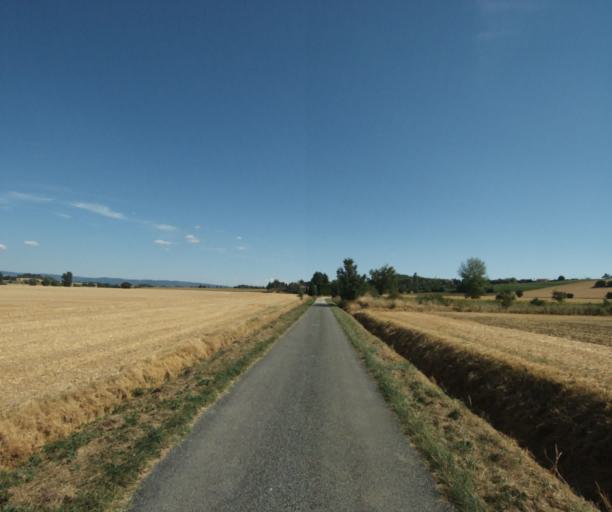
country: FR
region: Midi-Pyrenees
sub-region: Departement de la Haute-Garonne
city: Saint-Felix-Lauragais
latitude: 43.5038
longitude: 1.8944
